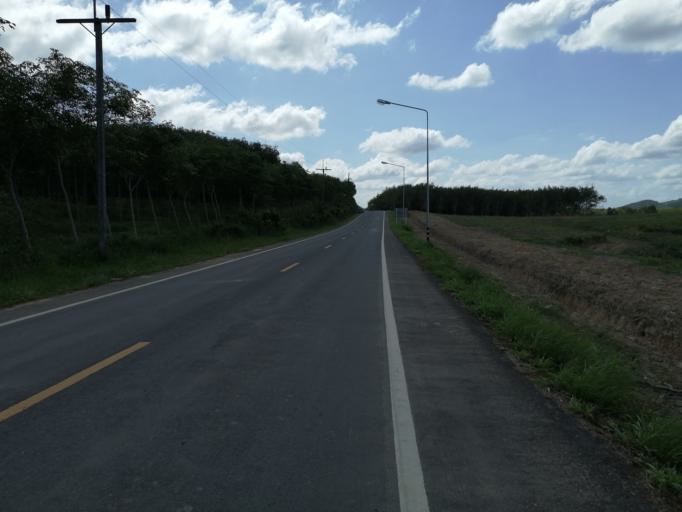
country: TH
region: Trang
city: Sikao
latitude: 7.6272
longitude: 99.3927
